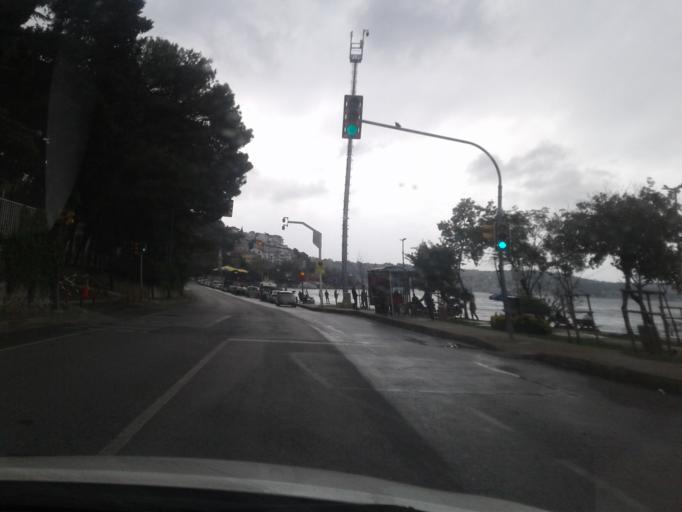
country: TR
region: Istanbul
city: UEskuedar
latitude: 41.0608
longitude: 29.0528
